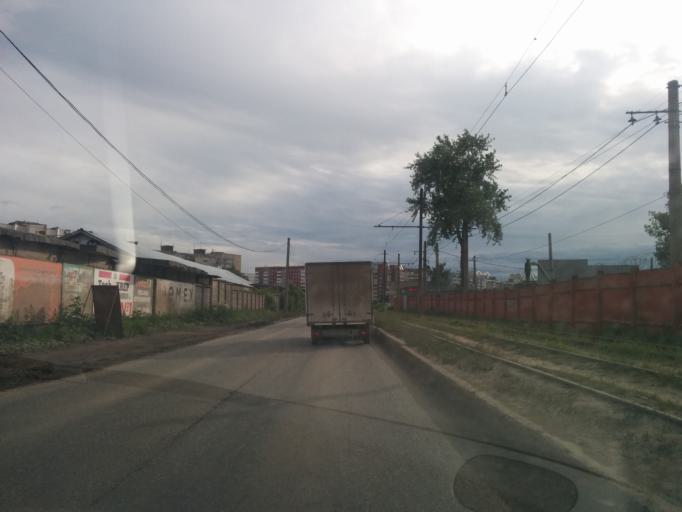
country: RU
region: Perm
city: Kondratovo
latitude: 58.0022
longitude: 56.1506
